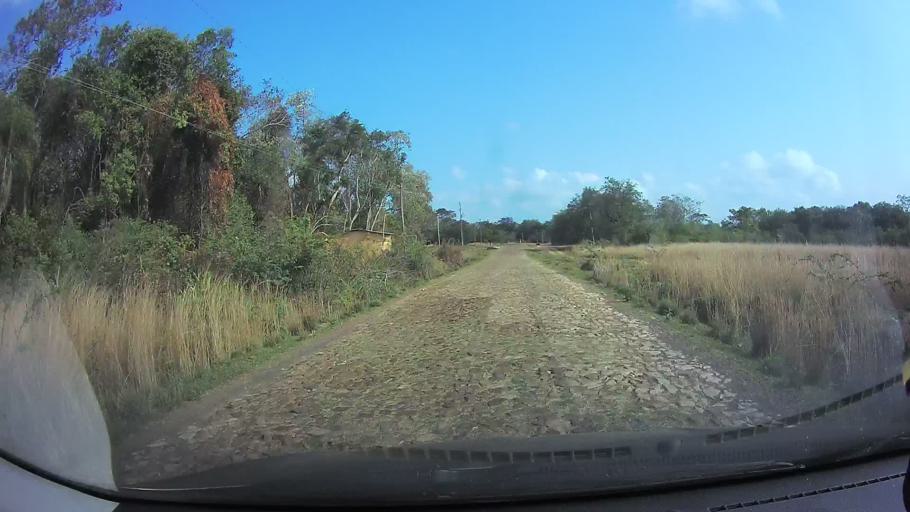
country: PY
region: Cordillera
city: Arroyos y Esteros
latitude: -24.9995
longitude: -57.1950
